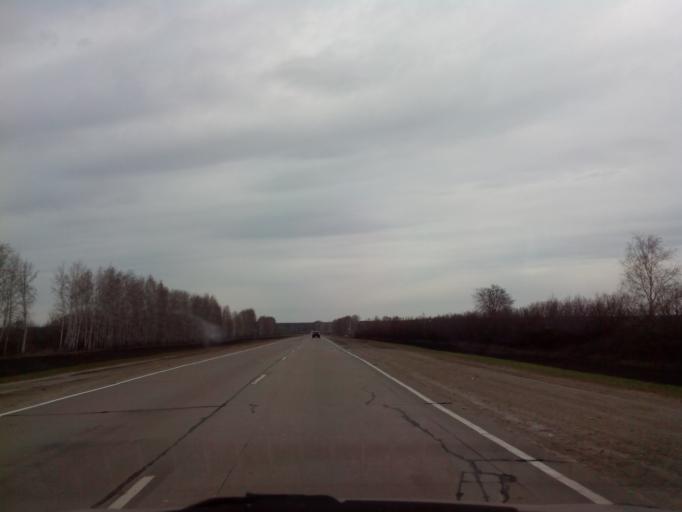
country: RU
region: Tambov
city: Znamenka
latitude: 52.5089
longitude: 41.3643
